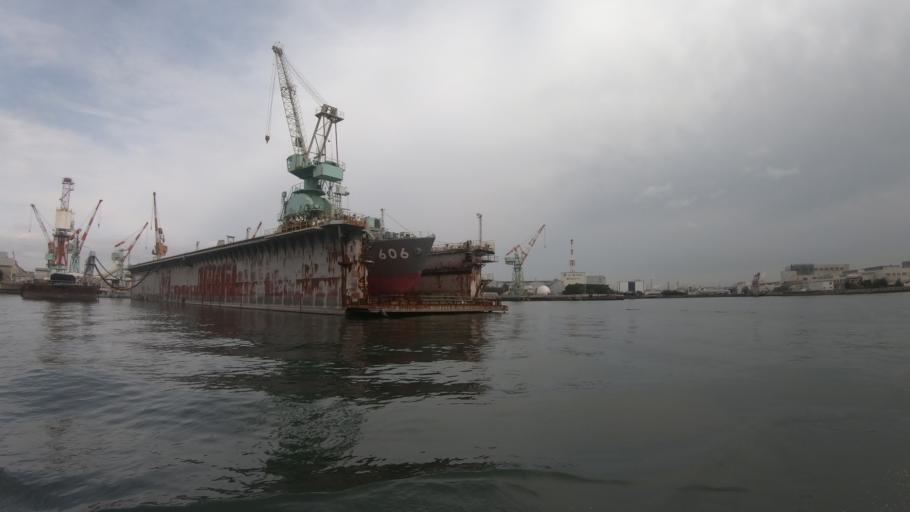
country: JP
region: Kanagawa
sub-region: Kawasaki-shi
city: Kawasaki
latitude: 35.4877
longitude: 139.6908
